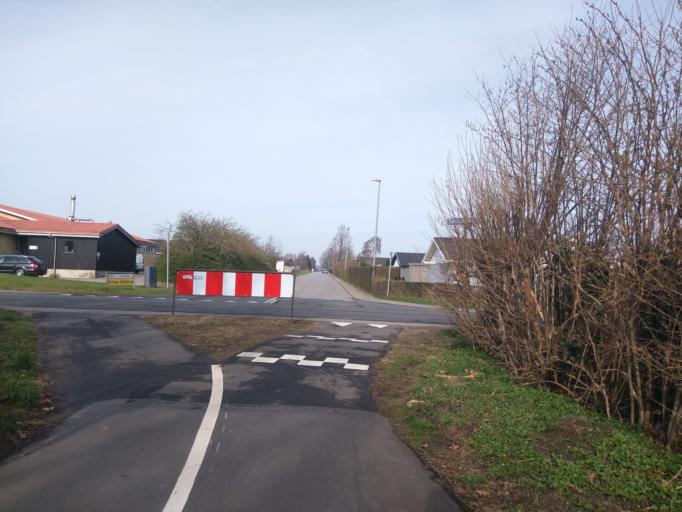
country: DK
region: South Denmark
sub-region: Fredericia Kommune
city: Snoghoj
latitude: 55.5448
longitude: 9.7042
